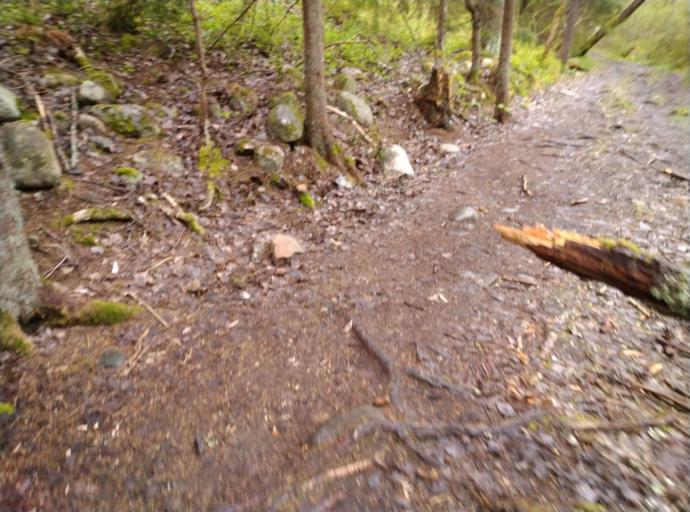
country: SE
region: Stockholm
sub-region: Nacka Kommun
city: Saltsjobaden
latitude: 59.2960
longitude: 18.2848
